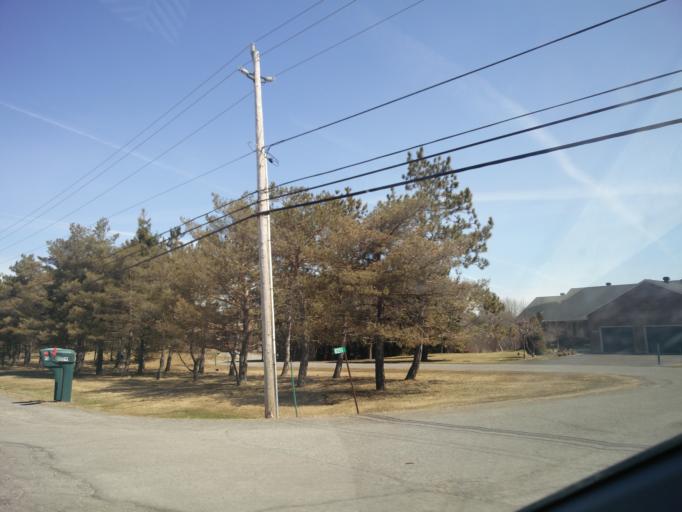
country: CA
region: Ontario
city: Bells Corners
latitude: 45.1882
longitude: -75.6386
